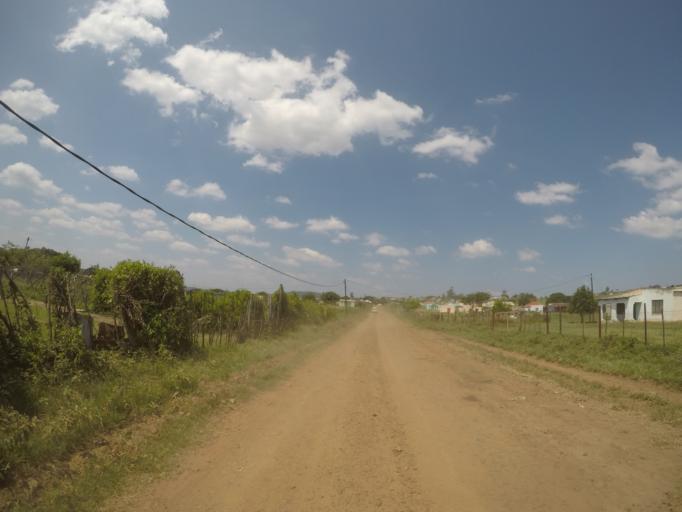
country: ZA
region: KwaZulu-Natal
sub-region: uThungulu District Municipality
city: Empangeni
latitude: -28.5884
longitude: 31.7375
